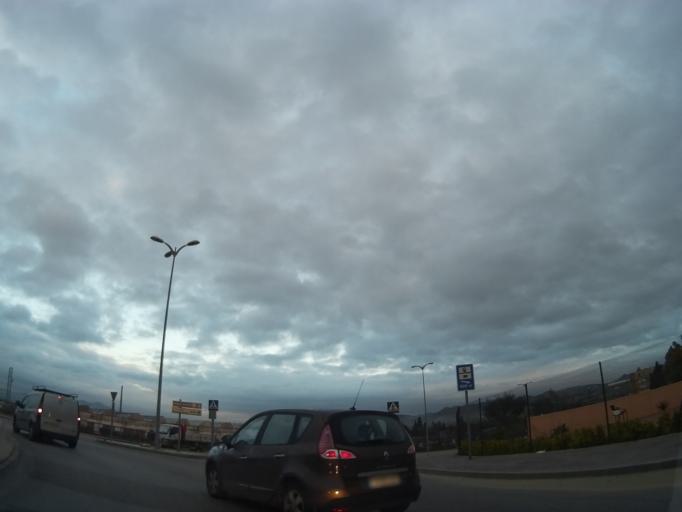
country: ES
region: Andalusia
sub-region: Provincia de Malaga
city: Malaga
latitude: 36.7035
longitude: -4.4927
